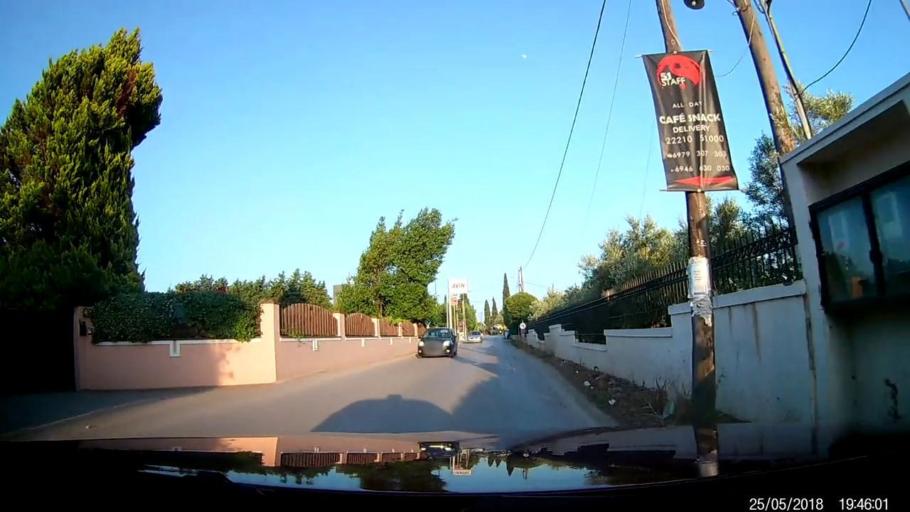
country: GR
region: Central Greece
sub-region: Nomos Evvoias
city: Ayios Nikolaos
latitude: 38.4291
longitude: 23.6375
